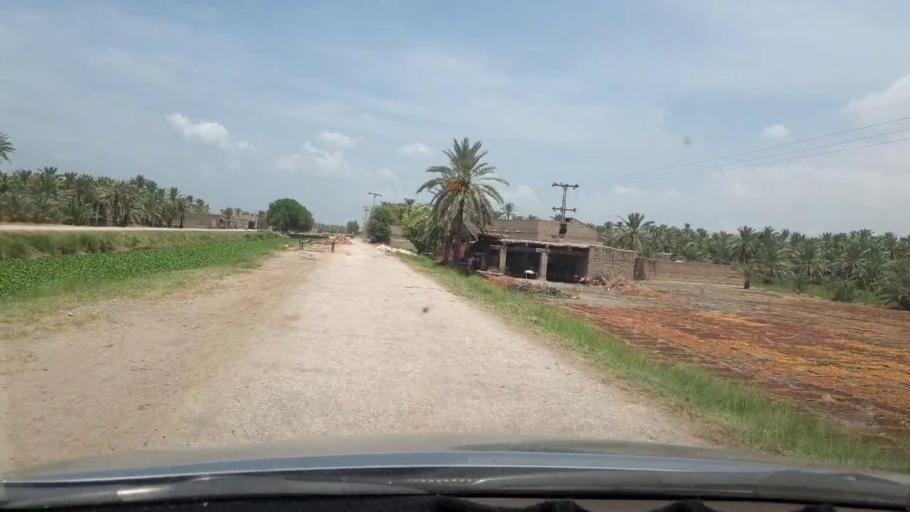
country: PK
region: Sindh
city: Khairpur
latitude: 27.4486
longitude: 68.7860
